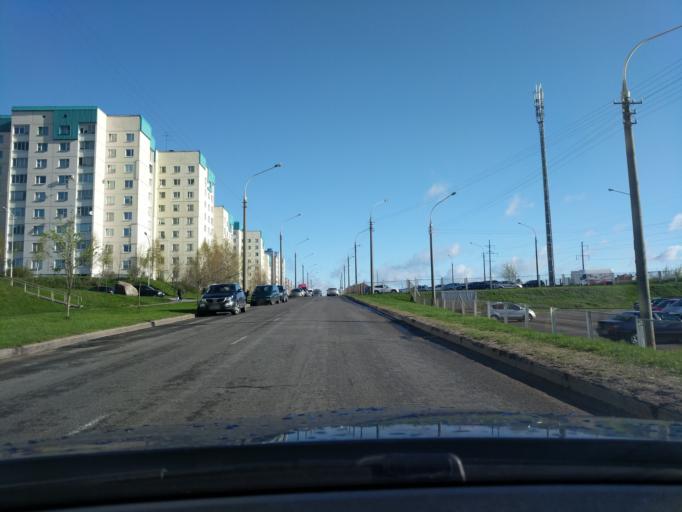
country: BY
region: Minsk
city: Novoye Medvezhino
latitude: 53.8959
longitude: 27.4630
